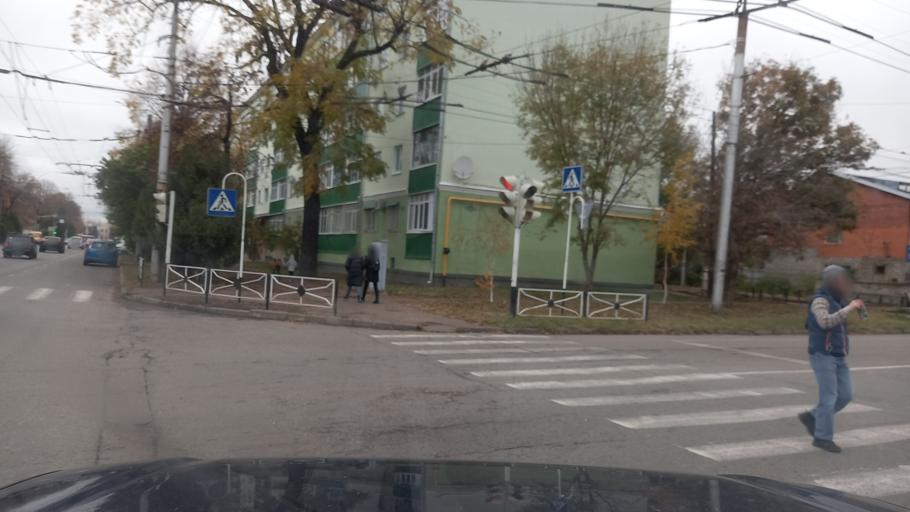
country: RU
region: Adygeya
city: Maykop
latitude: 44.6154
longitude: 40.1090
